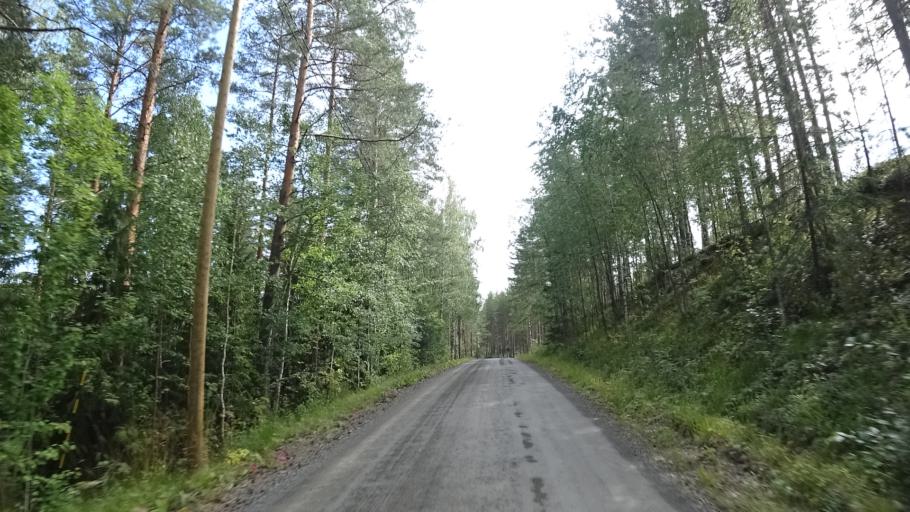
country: FI
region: North Karelia
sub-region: Joensuu
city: Pyhaeselkae
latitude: 62.3828
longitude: 29.8049
